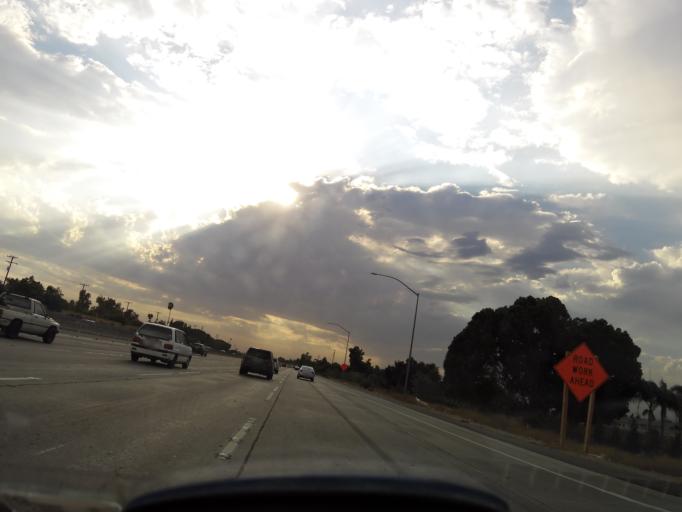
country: US
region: California
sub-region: Orange County
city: Yorba Linda
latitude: 33.8546
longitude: -117.7983
